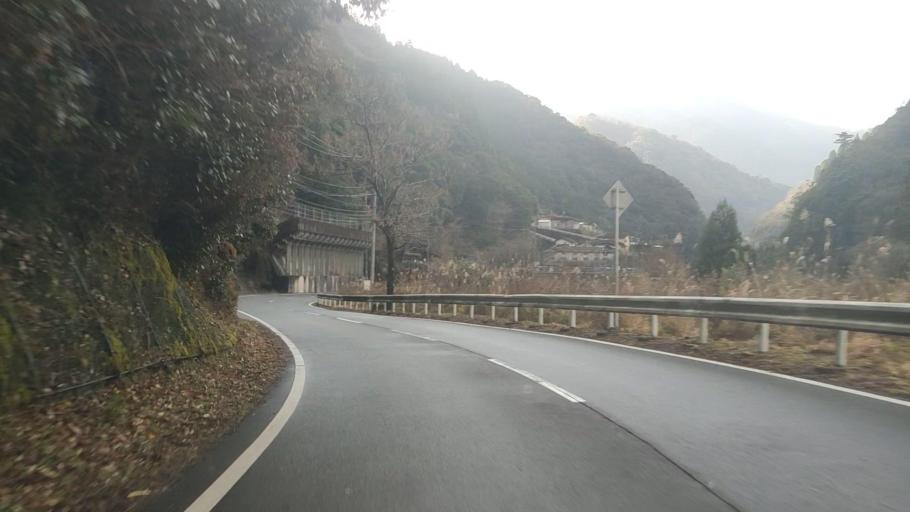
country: JP
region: Kumamoto
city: Hitoyoshi
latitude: 32.4292
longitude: 130.8583
